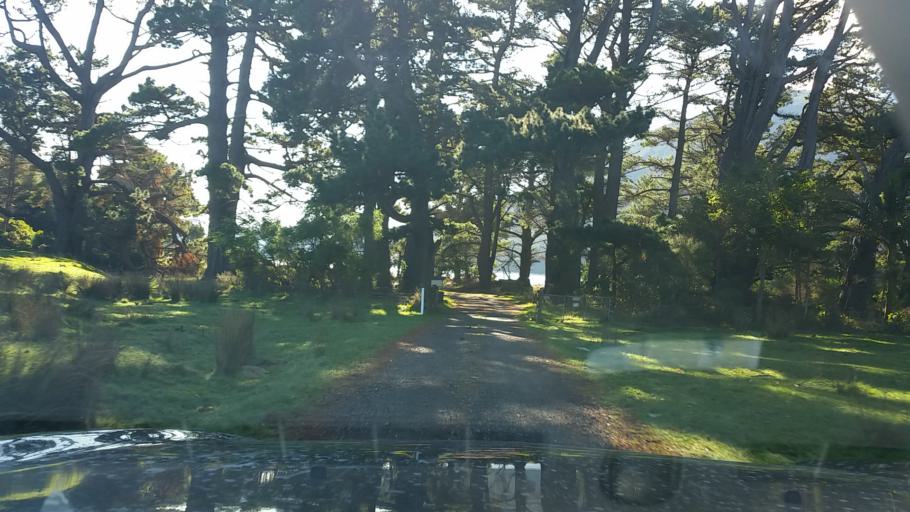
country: NZ
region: Marlborough
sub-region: Marlborough District
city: Picton
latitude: -41.1141
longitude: 174.0353
